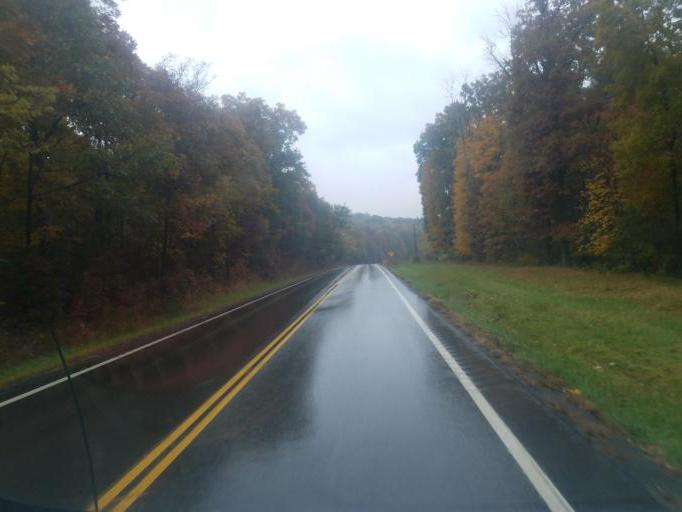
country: US
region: Ohio
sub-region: Muskingum County
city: Frazeysburg
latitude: 40.2239
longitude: -82.2643
